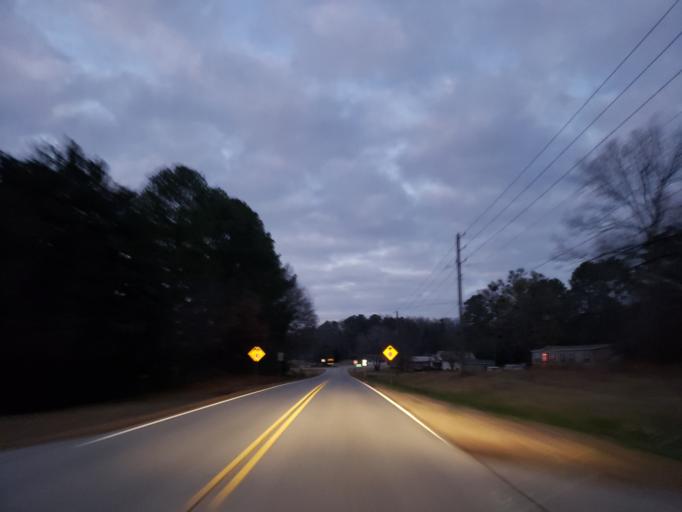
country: US
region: Georgia
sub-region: Carroll County
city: Temple
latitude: 33.8260
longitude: -85.0445
